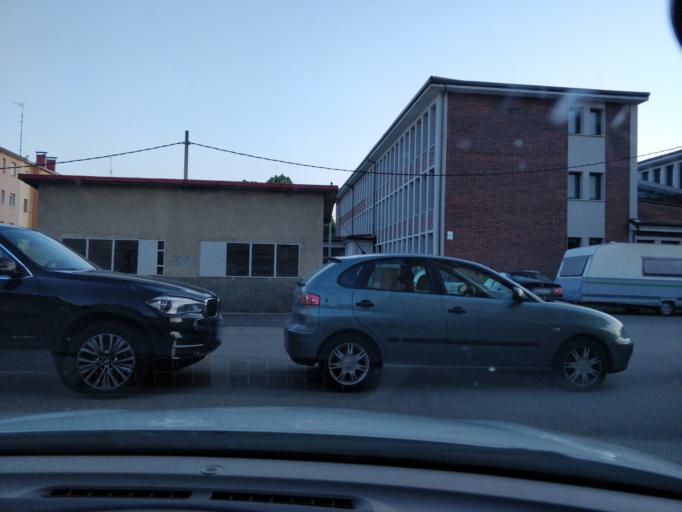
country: ES
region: Castille and Leon
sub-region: Provincia de Burgos
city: Medina de Pomar
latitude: 42.9416
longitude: -3.5702
